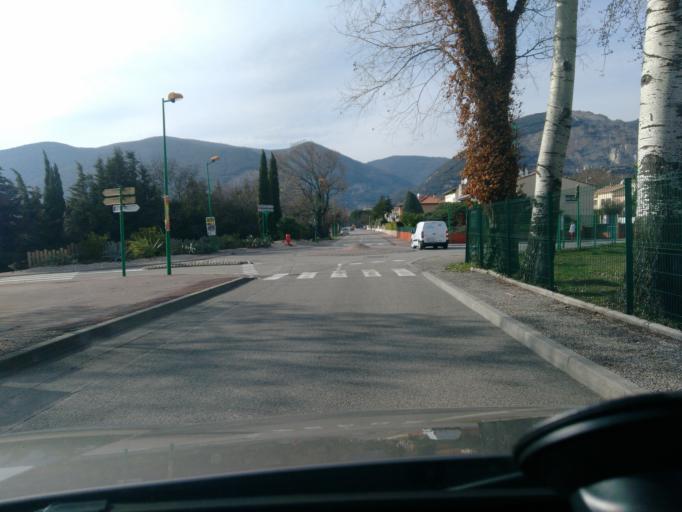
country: FR
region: Rhone-Alpes
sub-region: Departement de l'Ardeche
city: Cruas
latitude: 44.6555
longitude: 4.7751
